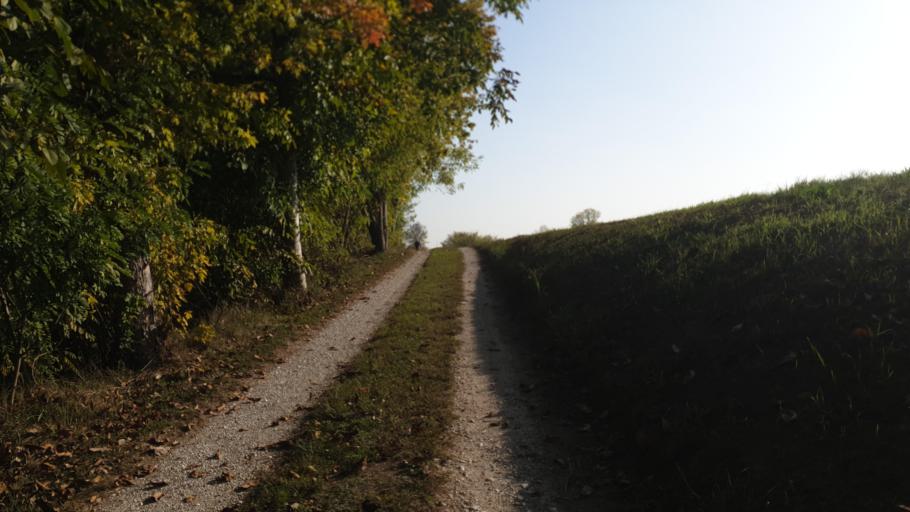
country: IT
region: Veneto
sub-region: Provincia di Venezia
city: Vigonovo
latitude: 45.3971
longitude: 12.0081
